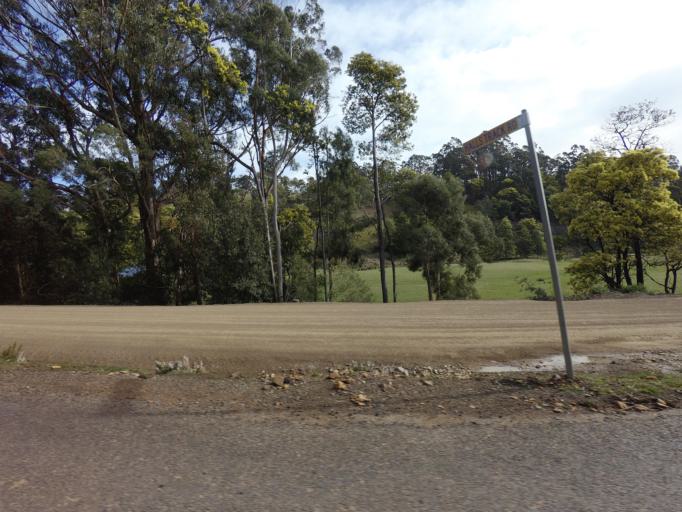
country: AU
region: Tasmania
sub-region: Kingborough
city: Margate
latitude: -43.0003
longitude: 147.1771
